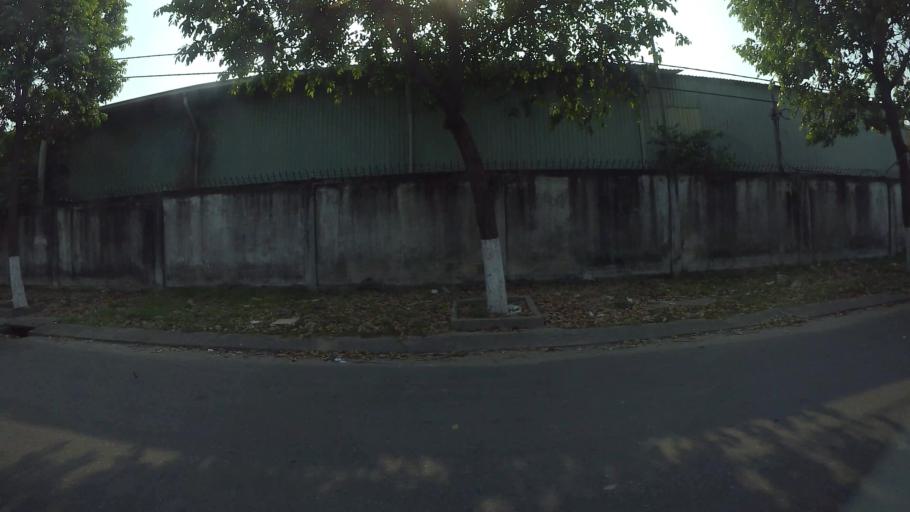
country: VN
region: Da Nang
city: Thanh Khe
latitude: 16.0548
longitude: 108.1743
